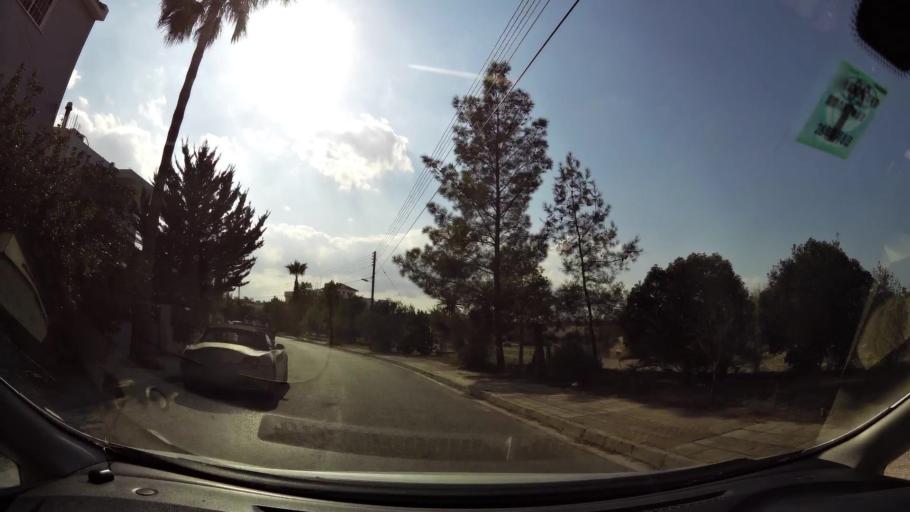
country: CY
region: Lefkosia
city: Kato Deftera
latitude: 35.1500
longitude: 33.2995
